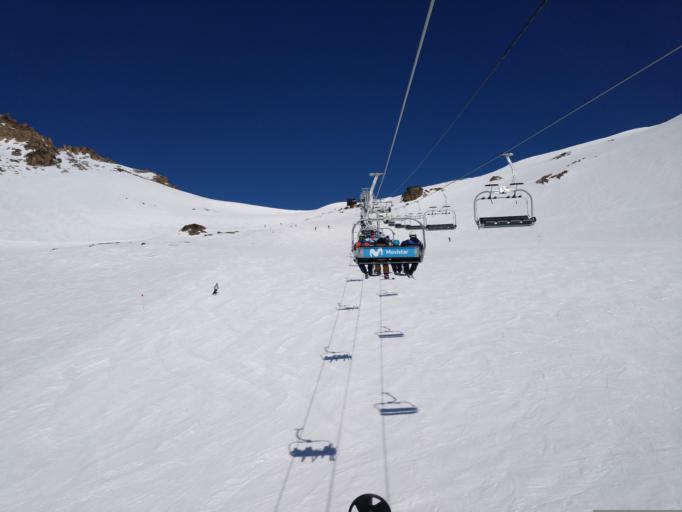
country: AR
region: Rio Negro
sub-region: Departamento de Bariloche
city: San Carlos de Bariloche
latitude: -41.1716
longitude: -71.4808
